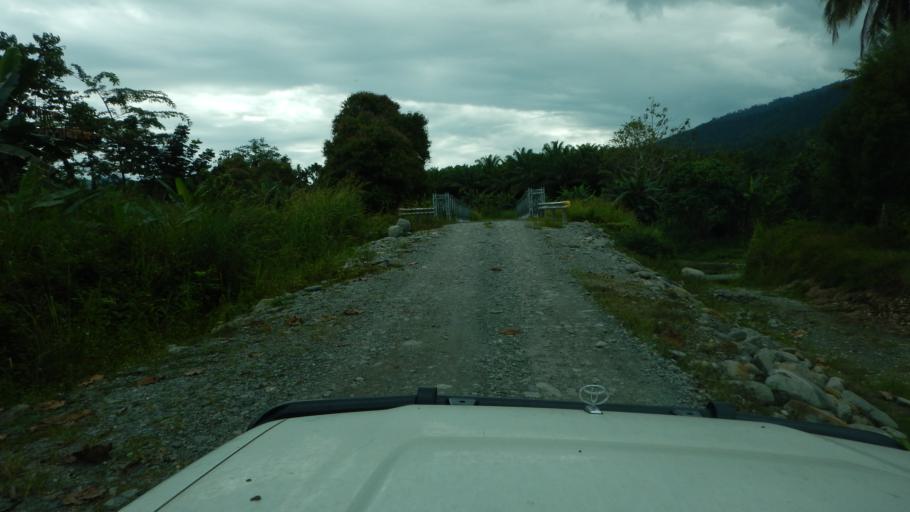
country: PG
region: Northern Province
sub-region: Sohe
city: Kokoda
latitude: -8.9180
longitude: 147.8701
